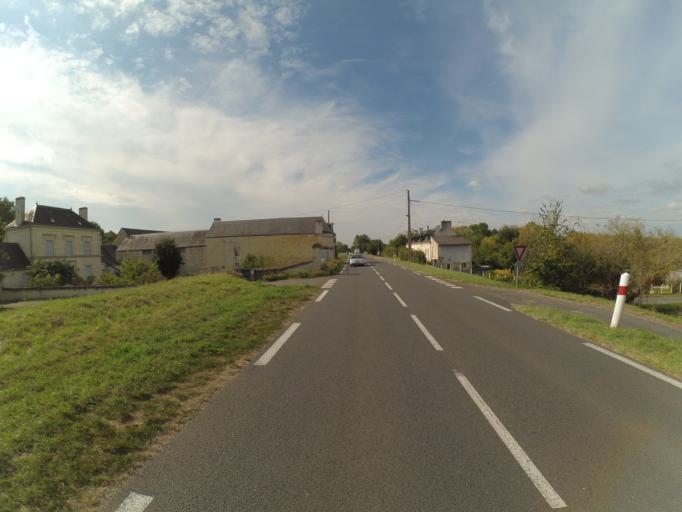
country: FR
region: Centre
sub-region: Departement d'Indre-et-Loire
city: Chouze-sur-Loire
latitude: 47.2417
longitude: 0.1412
